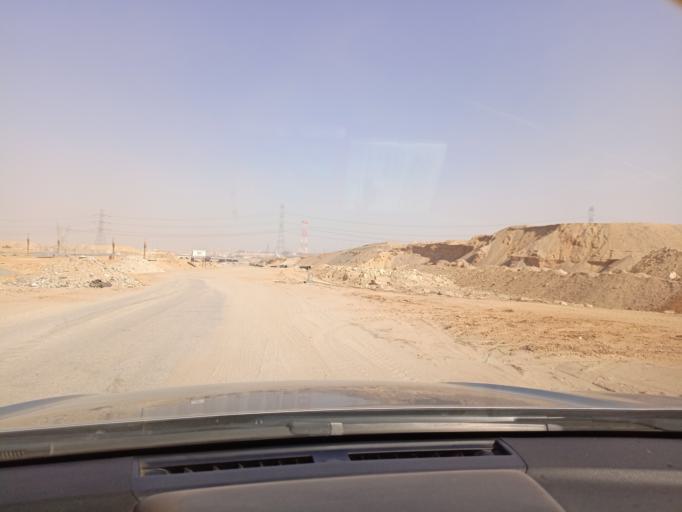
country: EG
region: Muhafazat al Qalyubiyah
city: Al Khankah
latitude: 30.0184
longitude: 31.7045
